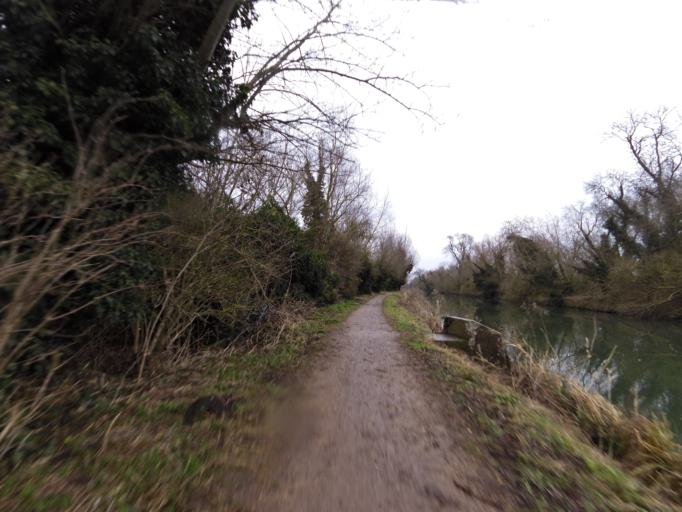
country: GB
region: England
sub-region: Cambridgeshire
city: Waterbeach
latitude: 52.2522
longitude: 0.1881
